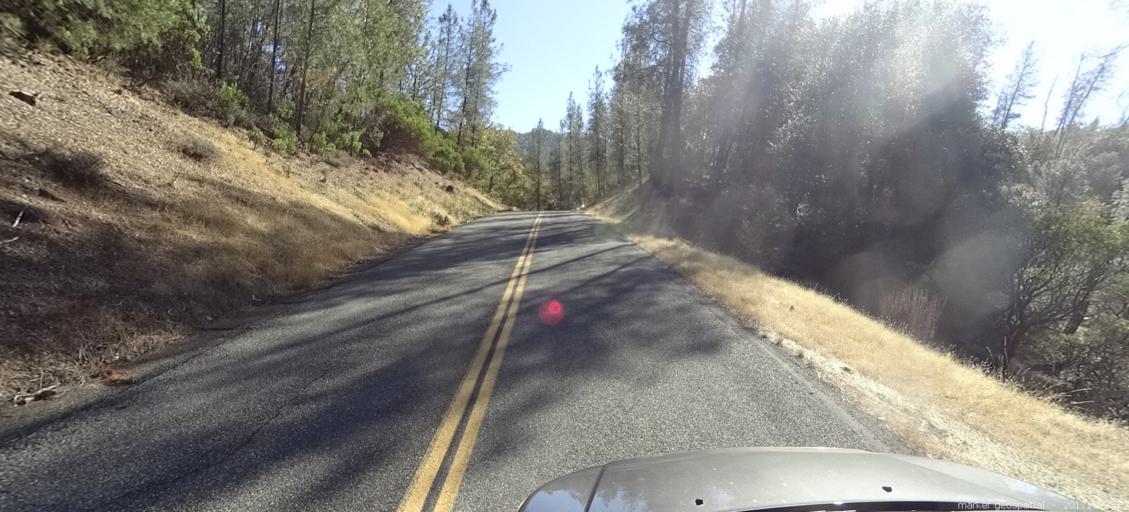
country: US
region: California
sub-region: Shasta County
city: Shasta
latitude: 40.6145
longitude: -122.5776
